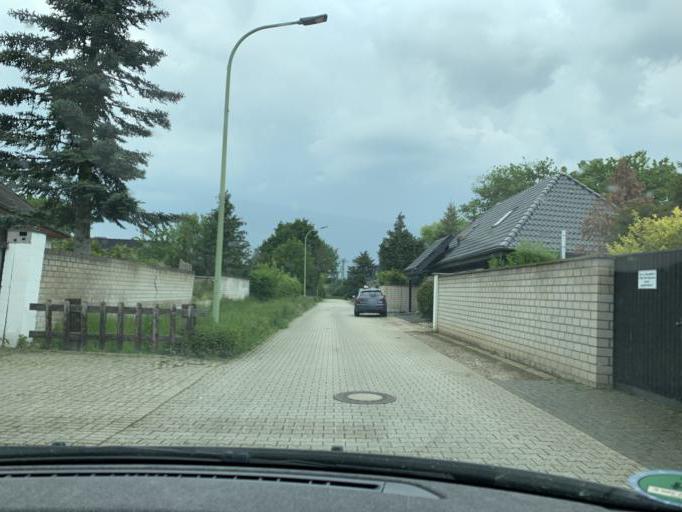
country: DE
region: North Rhine-Westphalia
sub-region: Regierungsbezirk Koln
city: Norvenich
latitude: 50.8152
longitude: 6.6803
